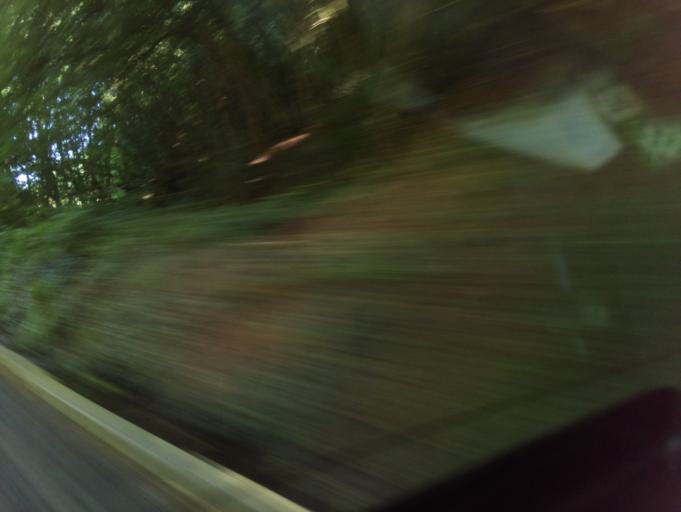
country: GB
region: England
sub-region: Gloucestershire
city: Coleford
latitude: 51.7941
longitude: -2.6640
